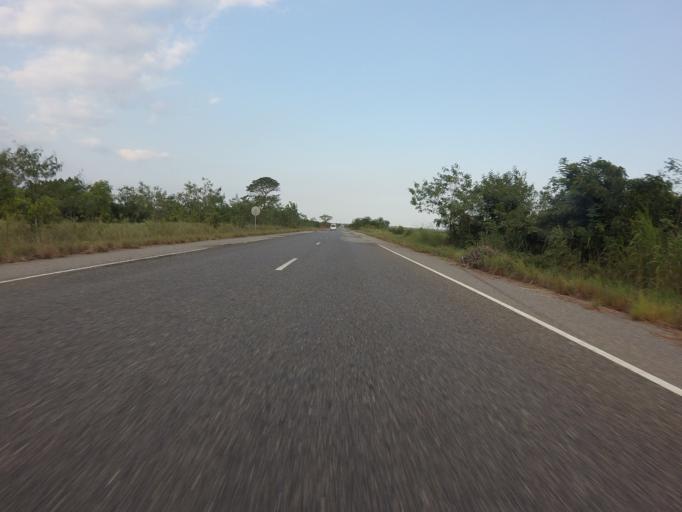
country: GH
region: Volta
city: Anloga
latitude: 6.0844
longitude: 0.5581
